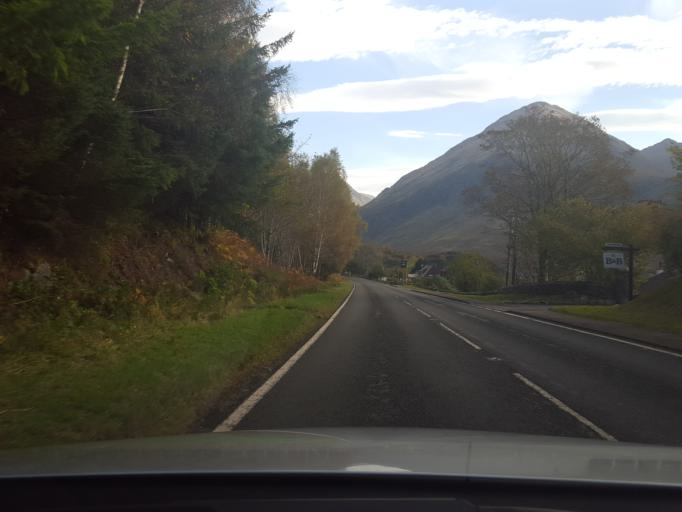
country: GB
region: Scotland
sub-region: Highland
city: Fort William
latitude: 57.2340
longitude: -5.4251
